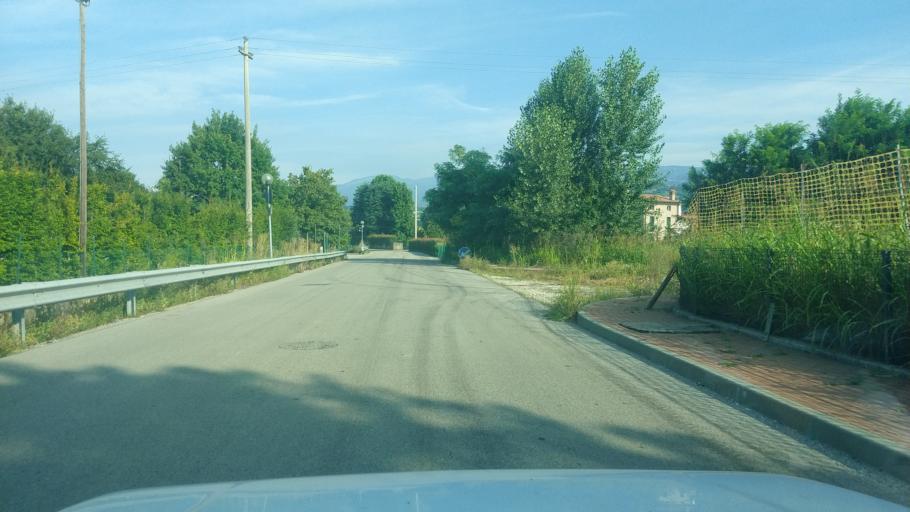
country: IT
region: Veneto
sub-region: Provincia di Vicenza
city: Mason Vicentino
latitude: 45.7217
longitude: 11.6224
